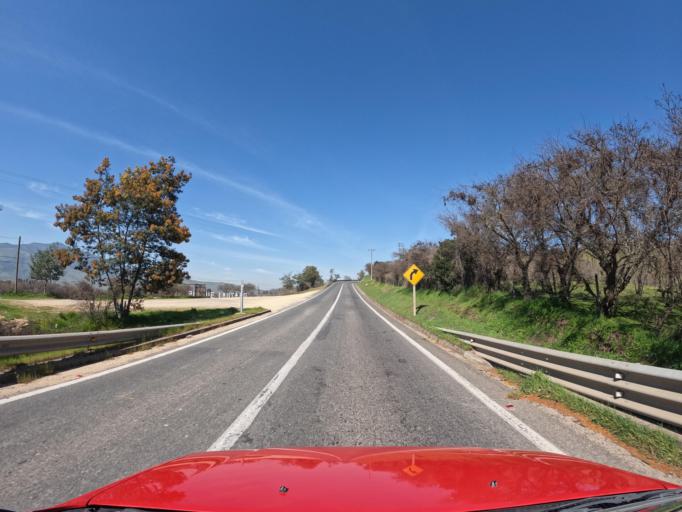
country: CL
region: Maule
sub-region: Provincia de Curico
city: Rauco
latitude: -35.0750
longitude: -71.6272
